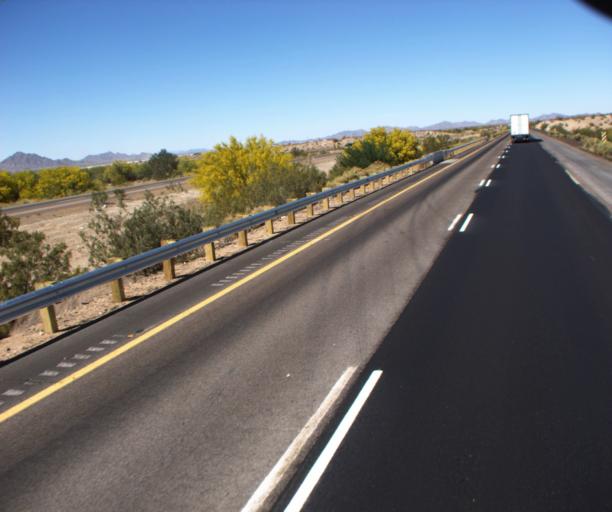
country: US
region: Arizona
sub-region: Maricopa County
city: Gila Bend
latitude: 33.0589
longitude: -112.6444
